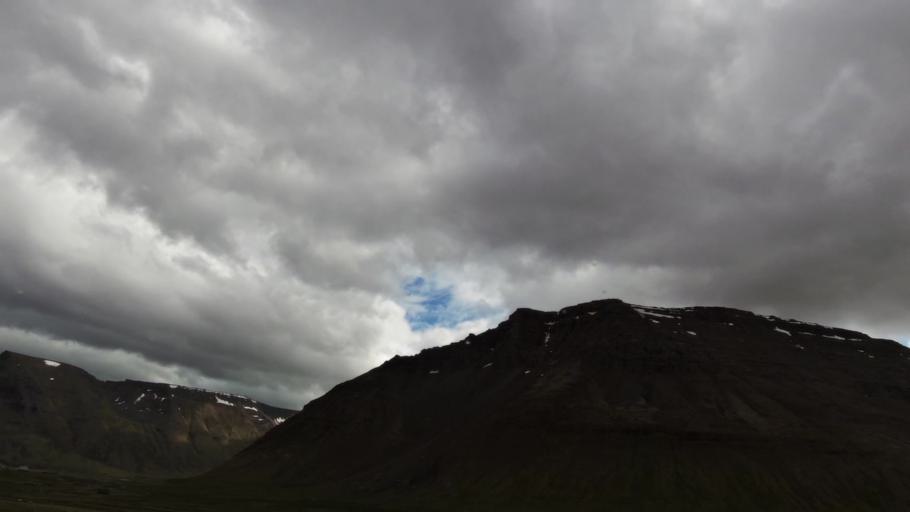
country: IS
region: Westfjords
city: Isafjoerdur
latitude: 66.1589
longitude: -23.2838
